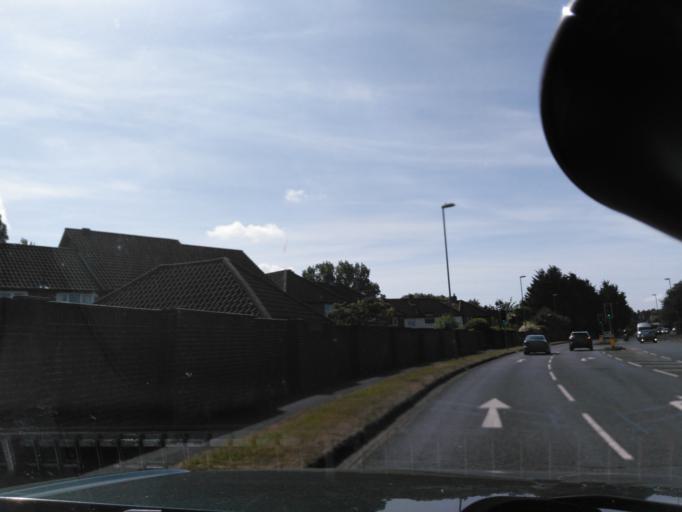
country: GB
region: England
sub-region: Hampshire
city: Lee-on-the-Solent
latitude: 50.8343
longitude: -1.2199
